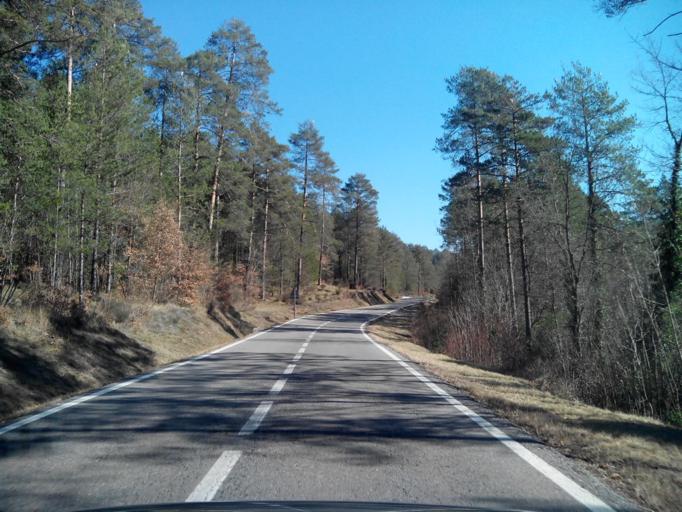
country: ES
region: Catalonia
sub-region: Provincia de Barcelona
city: Vilada
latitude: 42.1300
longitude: 1.9603
